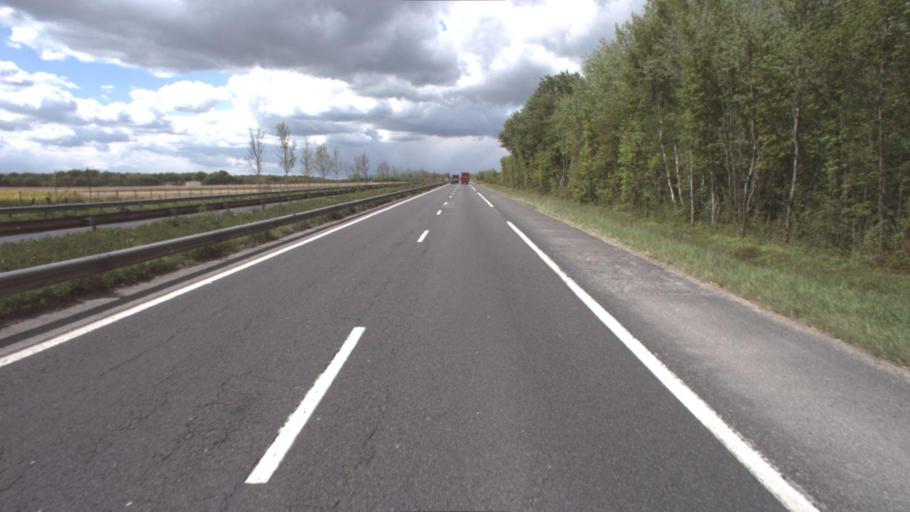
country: FR
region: Ile-de-France
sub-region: Departement de Seine-et-Marne
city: Neufmoutiers-en-Brie
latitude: 48.7242
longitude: 2.8283
